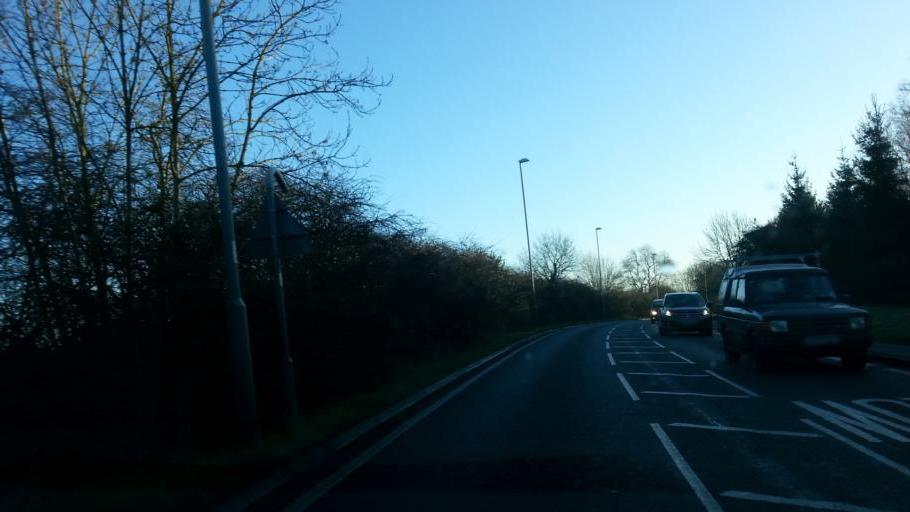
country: GB
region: England
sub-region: Nottinghamshire
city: South Collingham
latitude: 53.0816
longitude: -0.7573
